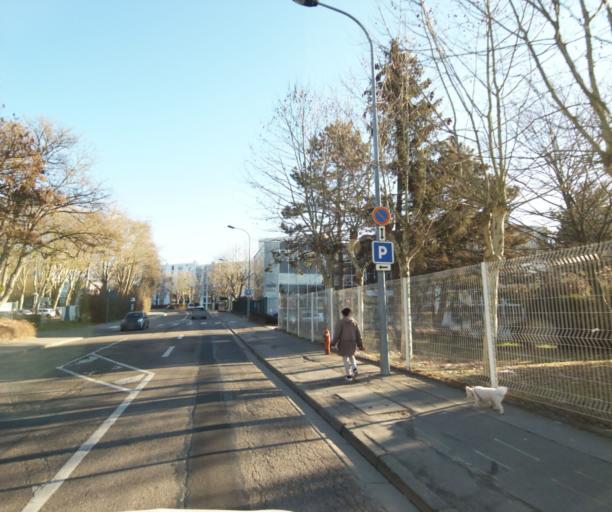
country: FR
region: Lorraine
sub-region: Departement de Meurthe-et-Moselle
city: Laxou
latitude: 48.6970
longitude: 6.1314
